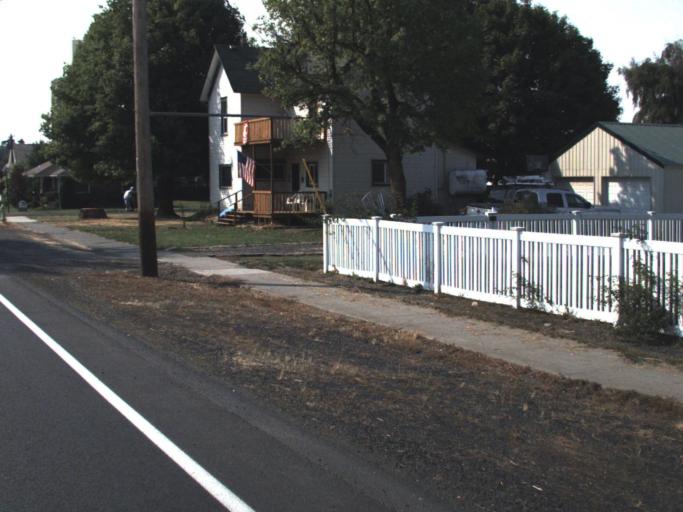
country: US
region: Washington
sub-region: Whitman County
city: Colfax
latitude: 47.0091
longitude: -117.1422
